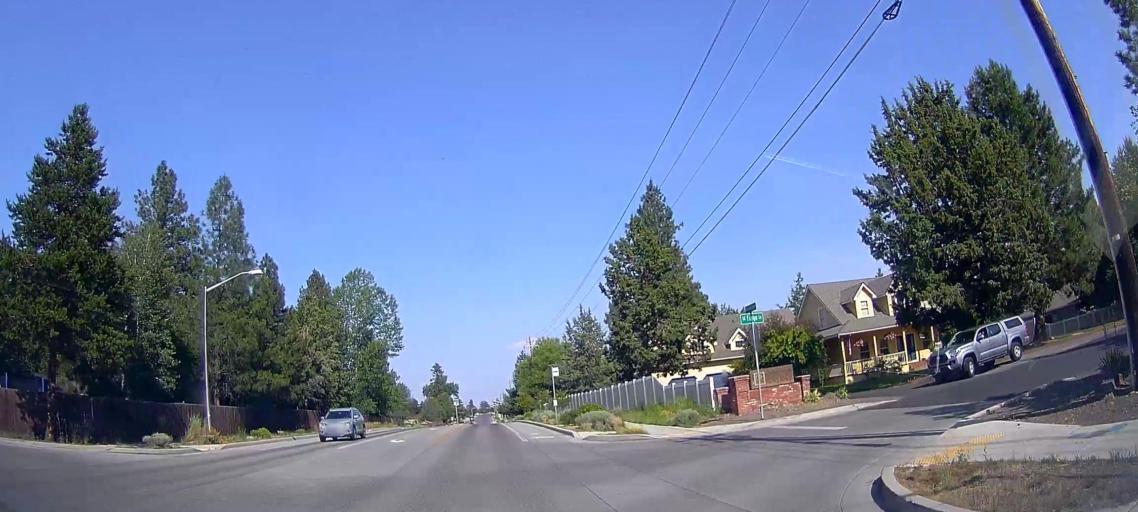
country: US
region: Oregon
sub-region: Deschutes County
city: Bend
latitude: 44.0371
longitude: -121.2728
